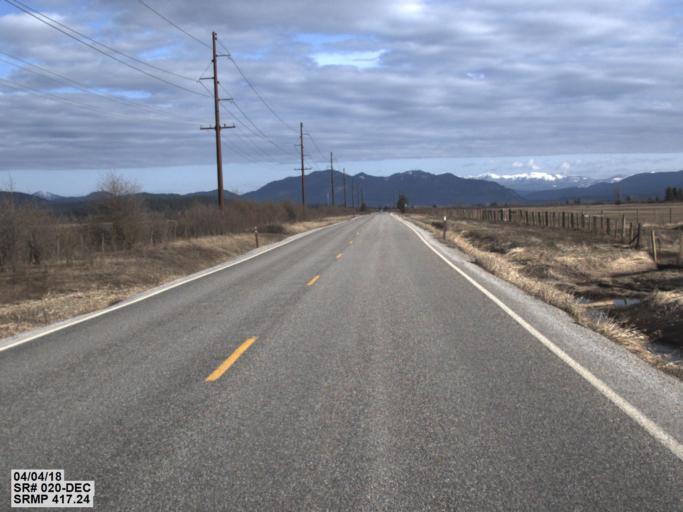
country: US
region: Washington
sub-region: Pend Oreille County
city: Newport
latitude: 48.3633
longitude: -117.3047
